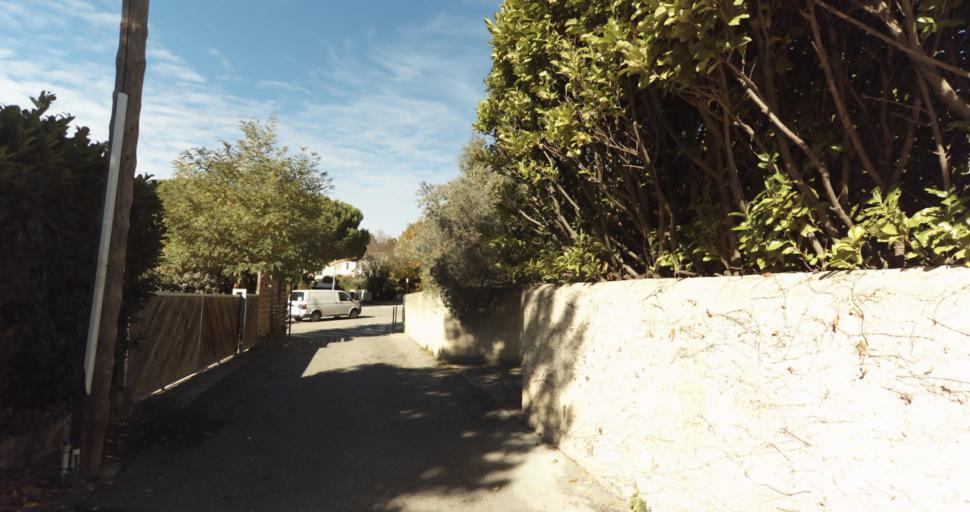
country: FR
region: Provence-Alpes-Cote d'Azur
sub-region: Departement des Bouches-du-Rhone
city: Venelles
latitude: 43.5966
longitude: 5.4763
